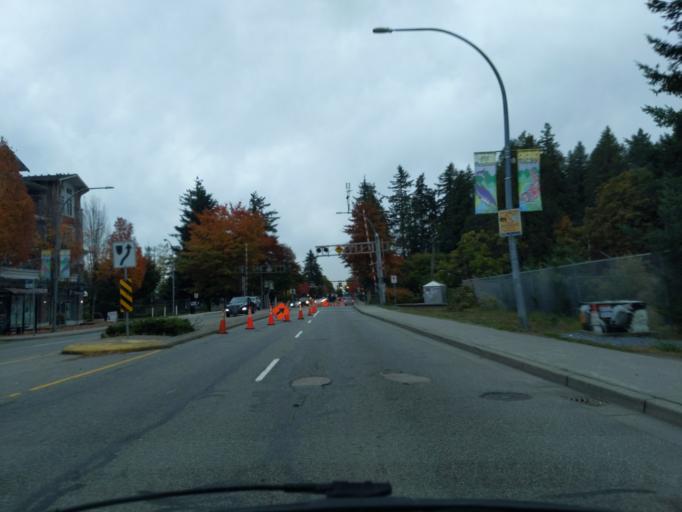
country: CA
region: British Columbia
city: Pitt Meadows
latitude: 49.2270
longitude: -122.6896
